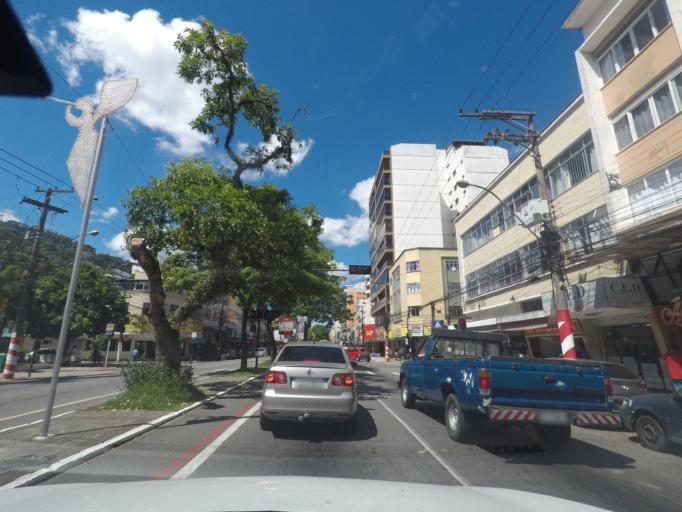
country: BR
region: Rio de Janeiro
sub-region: Teresopolis
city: Teresopolis
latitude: -22.4182
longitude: -42.9735
